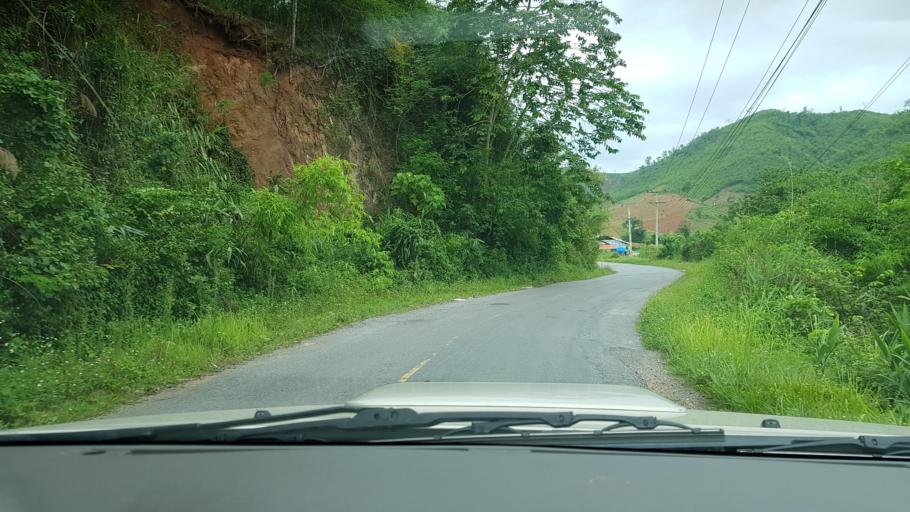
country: LA
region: Loungnamtha
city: Muang Nale
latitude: 20.3746
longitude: 101.7277
